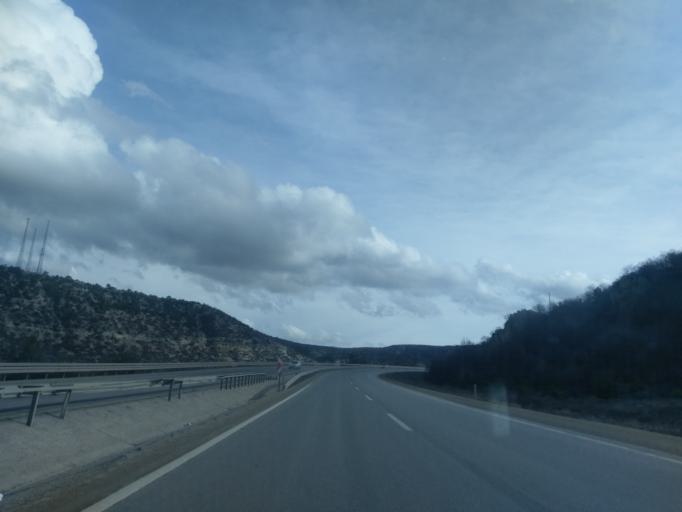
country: TR
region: Kuetahya
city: Sabuncu
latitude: 39.5636
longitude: 30.0741
